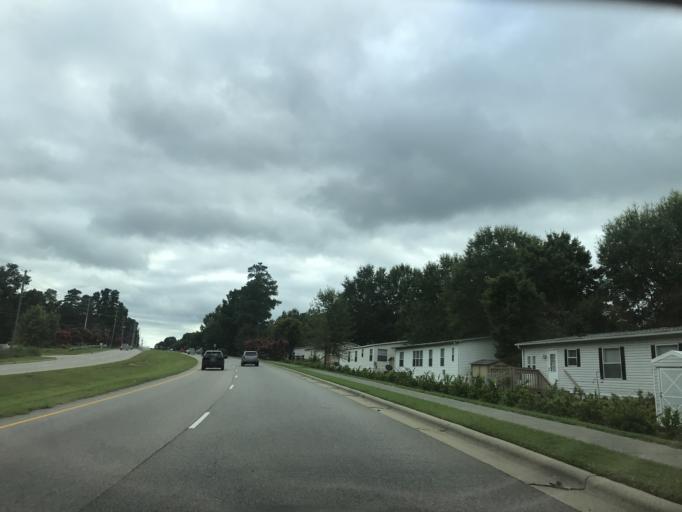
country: US
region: North Carolina
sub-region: Wake County
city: Garner
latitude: 35.7368
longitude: -78.5730
